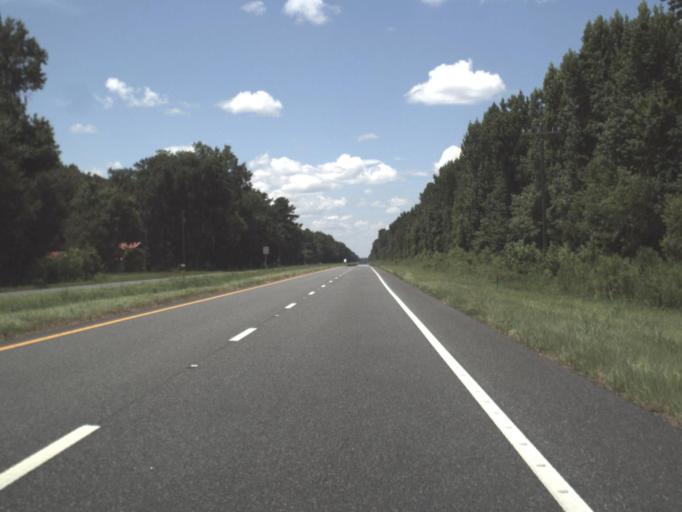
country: US
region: Florida
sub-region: Taylor County
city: Perry
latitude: 30.2749
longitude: -83.7222
